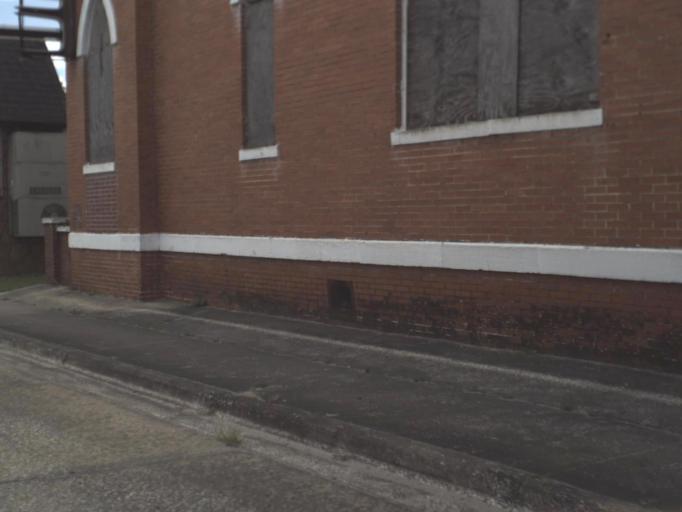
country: US
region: Florida
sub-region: Putnam County
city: Palatka
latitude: 29.6486
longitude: -81.6382
